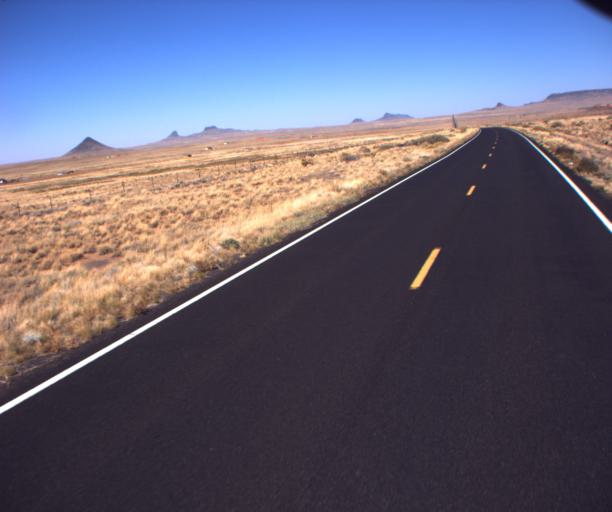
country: US
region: Arizona
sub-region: Navajo County
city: Dilkon
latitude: 35.3062
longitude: -110.4227
